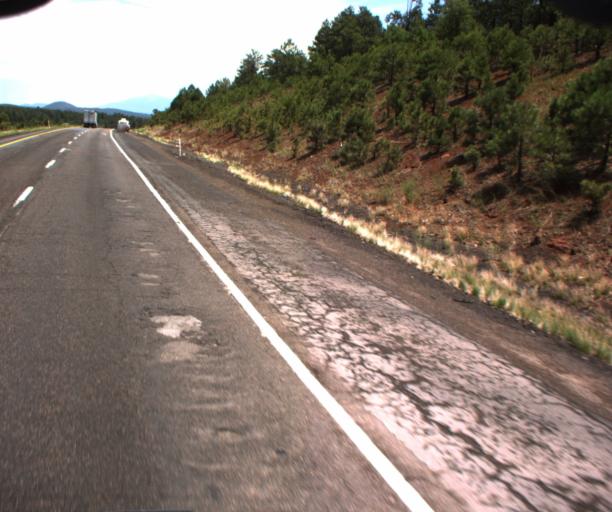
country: US
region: Arizona
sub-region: Coconino County
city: Parks
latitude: 35.2631
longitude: -112.0667
